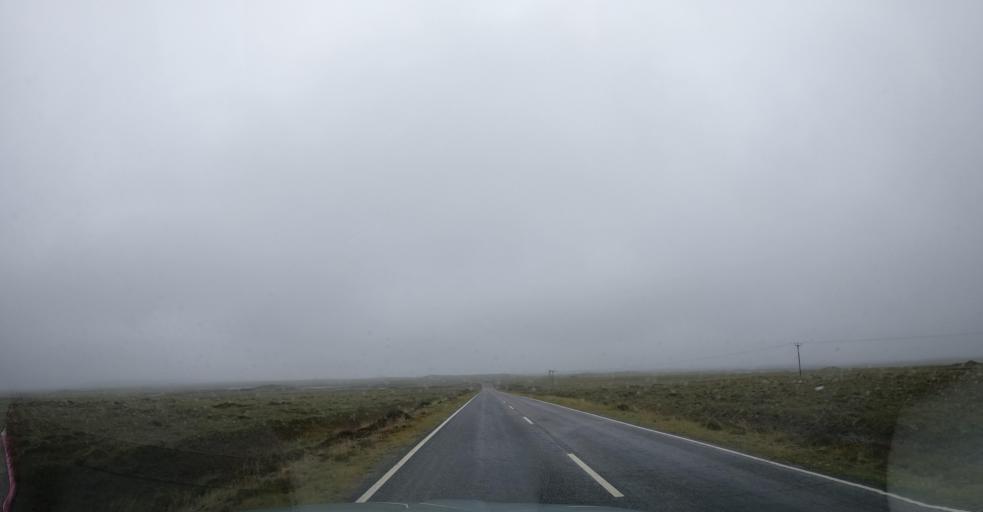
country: GB
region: Scotland
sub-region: Eilean Siar
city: Isle of North Uist
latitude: 57.5815
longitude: -7.2476
